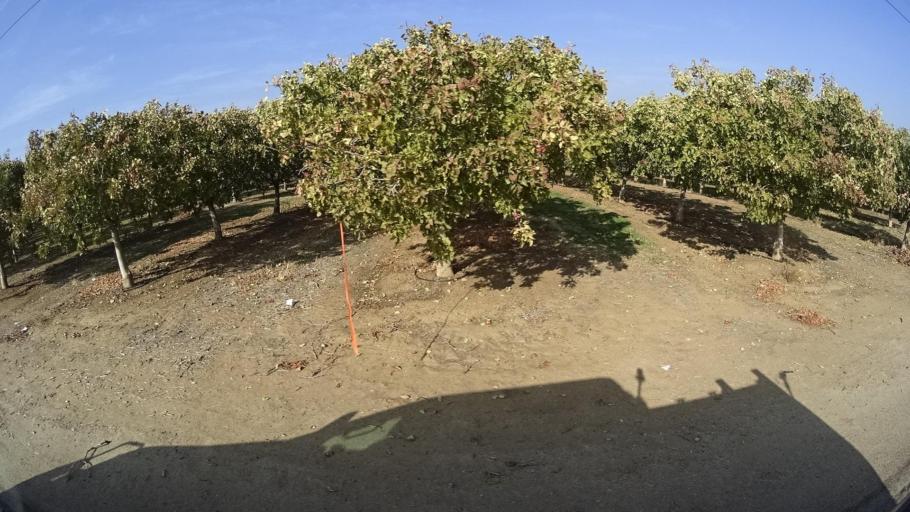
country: US
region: California
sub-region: Tulare County
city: Richgrove
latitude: 35.7908
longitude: -119.0738
